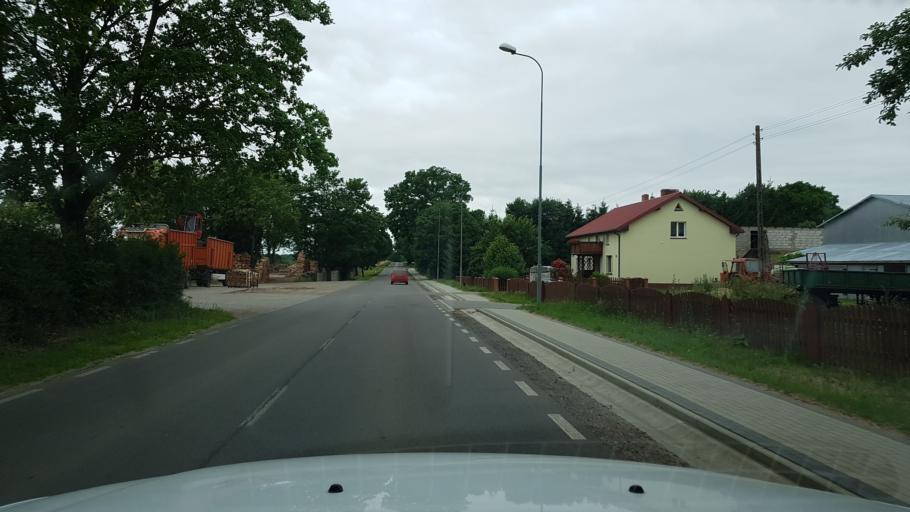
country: PL
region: West Pomeranian Voivodeship
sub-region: Powiat gryficki
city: Brojce
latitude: 53.9586
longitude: 15.3307
